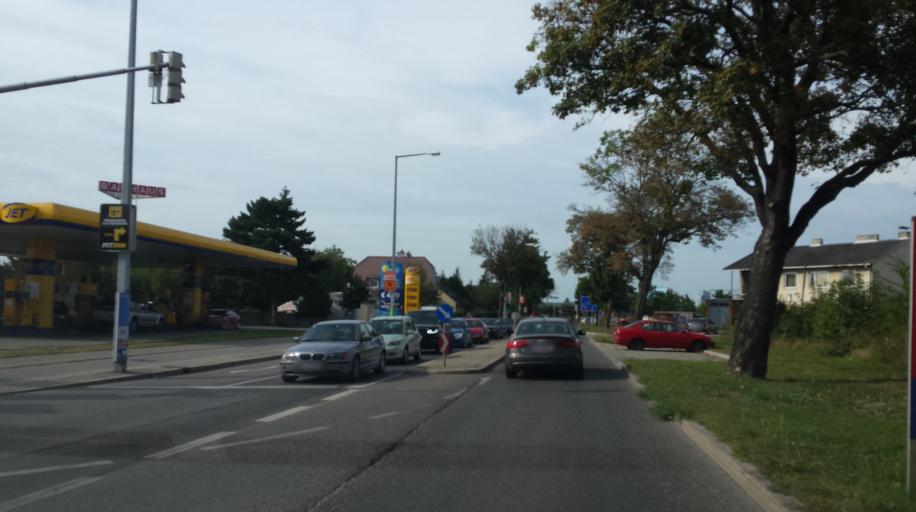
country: AT
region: Lower Austria
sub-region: Politischer Bezirk Wien-Umgebung
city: Gerasdorf bei Wien
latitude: 48.2378
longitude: 16.4613
